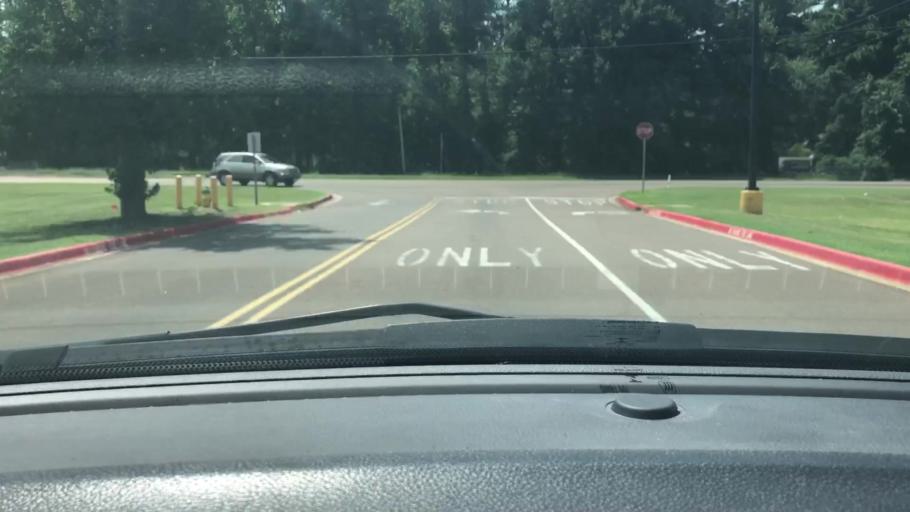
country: US
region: Texas
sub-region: Bowie County
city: Wake Village
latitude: 33.4439
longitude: -94.1006
